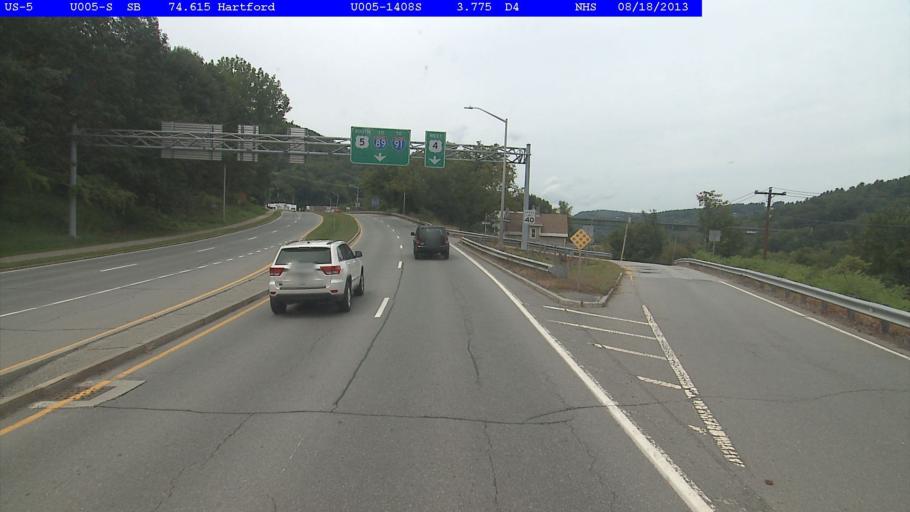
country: US
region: Vermont
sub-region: Windsor County
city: White River Junction
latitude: 43.6518
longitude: -72.3253
